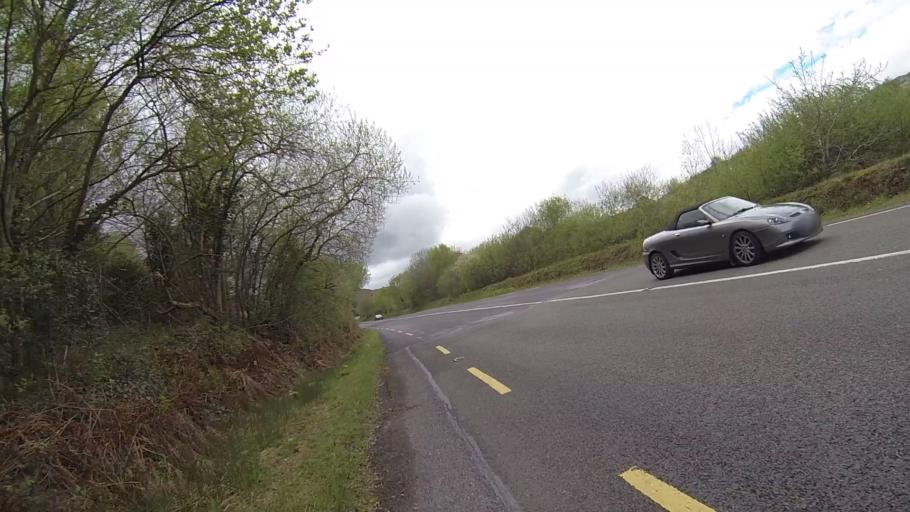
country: IE
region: Munster
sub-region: County Cork
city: Bantry
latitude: 51.7296
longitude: -9.5658
